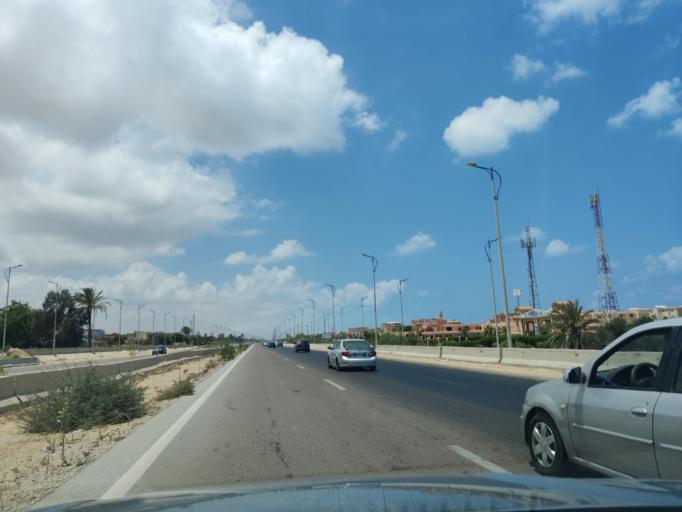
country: EG
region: Alexandria
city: Alexandria
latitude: 30.9396
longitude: 29.4974
